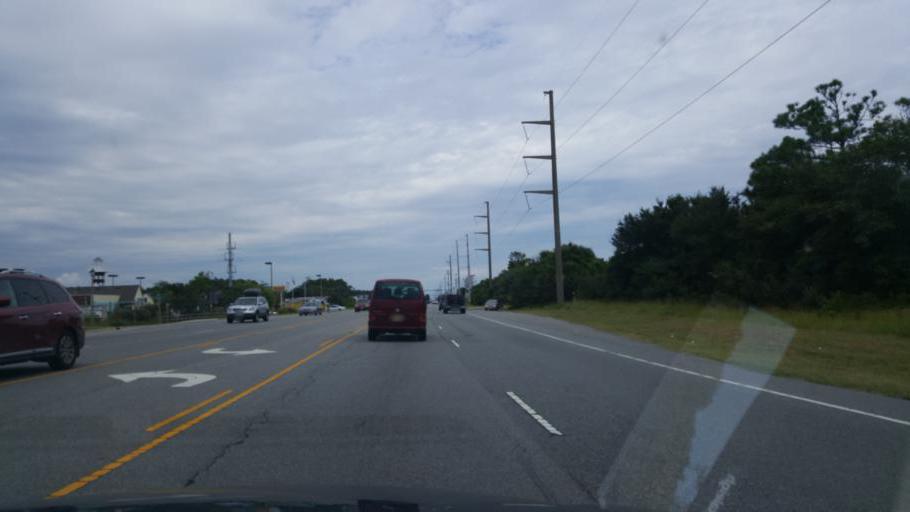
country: US
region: North Carolina
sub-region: Dare County
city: Nags Head
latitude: 35.9748
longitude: -75.6394
